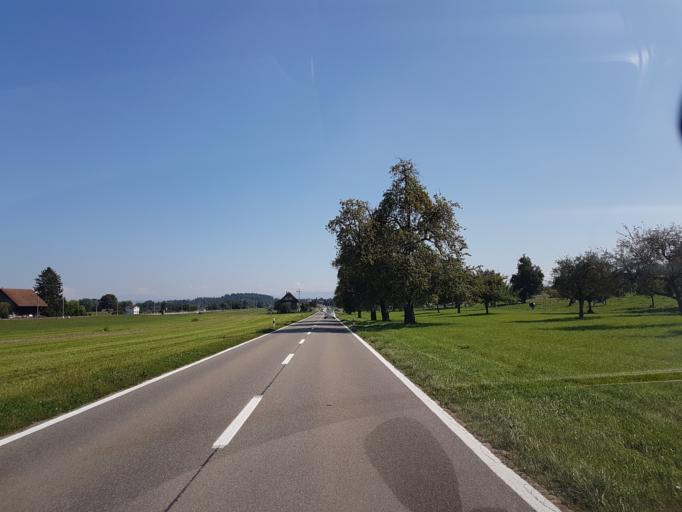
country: CH
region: Aargau
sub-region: Bezirk Muri
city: Muri
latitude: 47.2857
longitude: 8.3279
